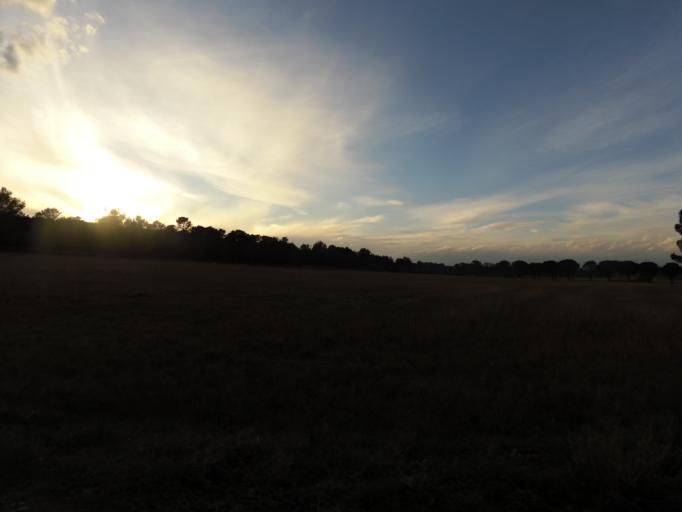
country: FR
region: Languedoc-Roussillon
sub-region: Departement du Gard
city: La Calmette
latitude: 43.8777
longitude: 4.2633
